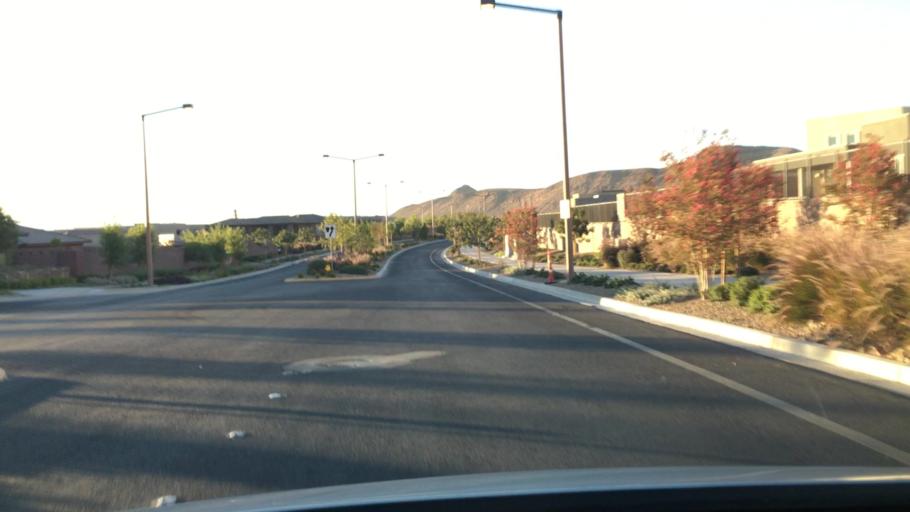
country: US
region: Nevada
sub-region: Clark County
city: Summerlin South
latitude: 36.0777
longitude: -115.3199
